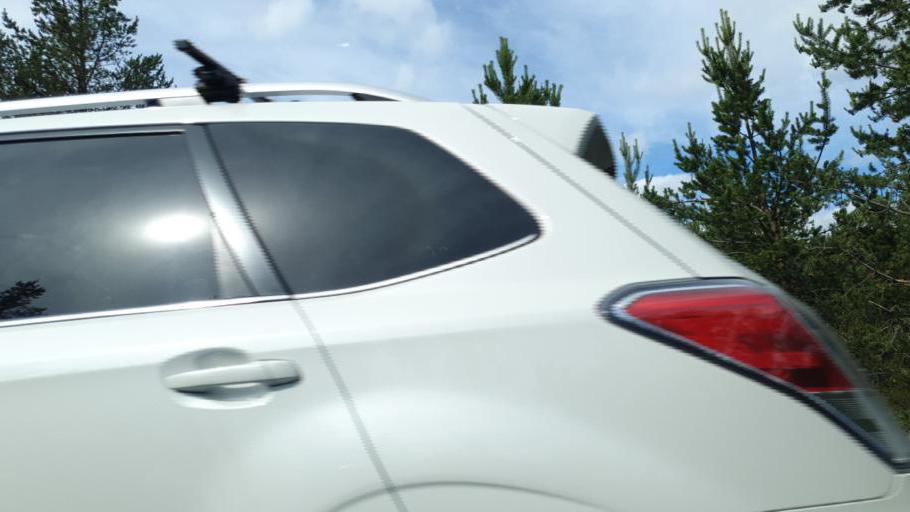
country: NO
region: Oppland
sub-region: Vaga
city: Vagamo
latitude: 61.7179
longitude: 9.0543
